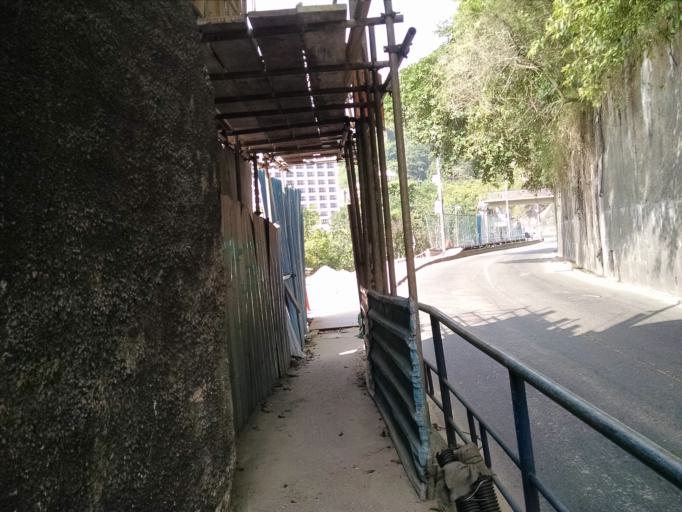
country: BR
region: Rio de Janeiro
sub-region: Rio De Janeiro
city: Rio de Janeiro
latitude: -22.9907
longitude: -43.2315
